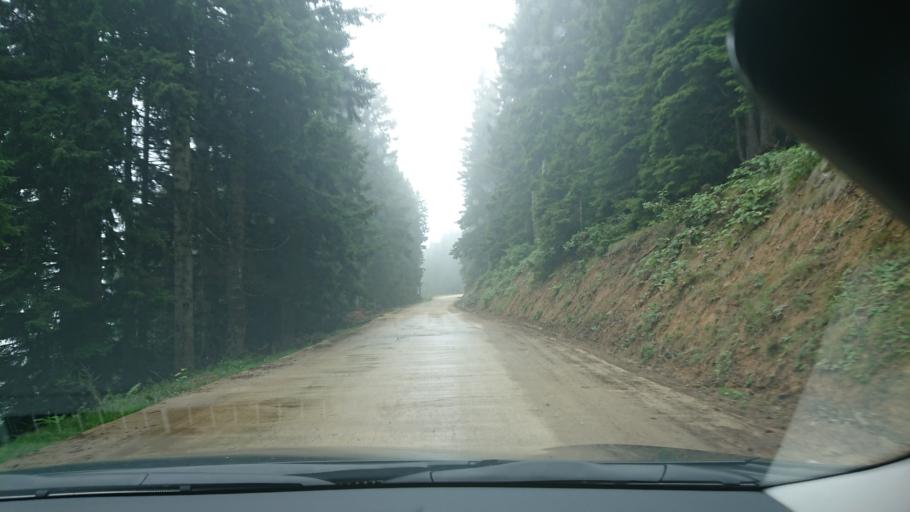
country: TR
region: Gumushane
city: Kurtun
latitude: 40.6685
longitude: 39.0119
